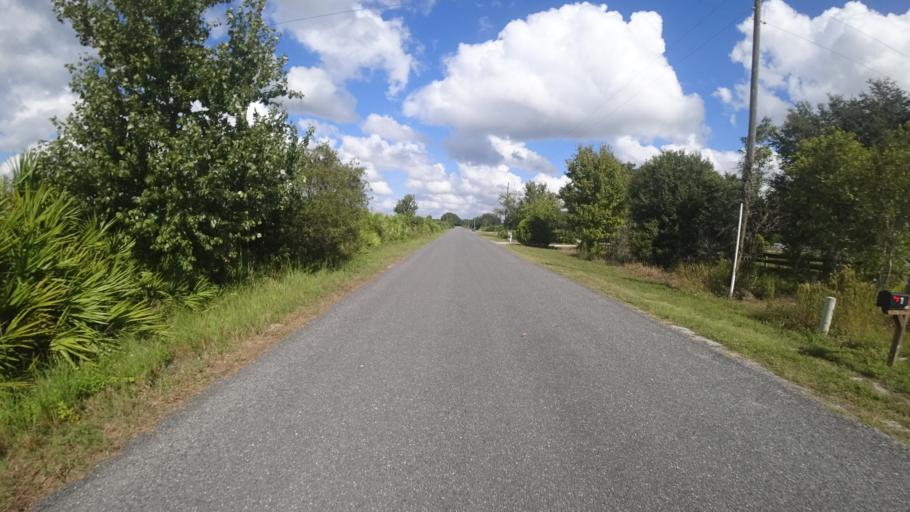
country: US
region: Florida
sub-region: Hillsborough County
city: Wimauma
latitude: 27.4668
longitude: -82.1702
